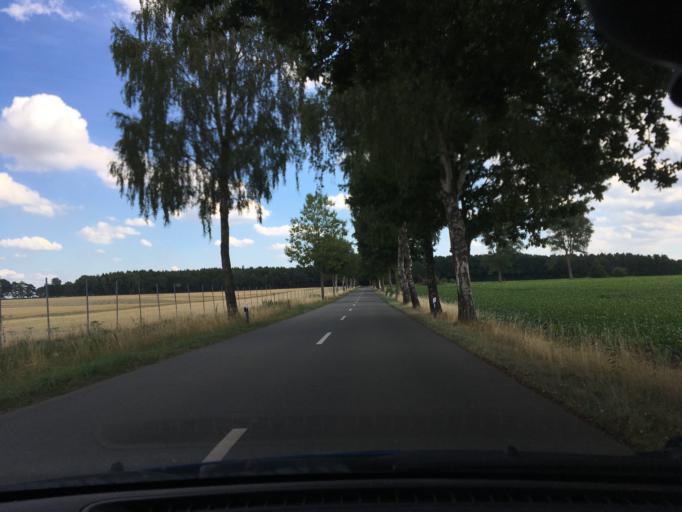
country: DE
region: Lower Saxony
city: Wriedel
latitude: 53.0520
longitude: 10.2502
